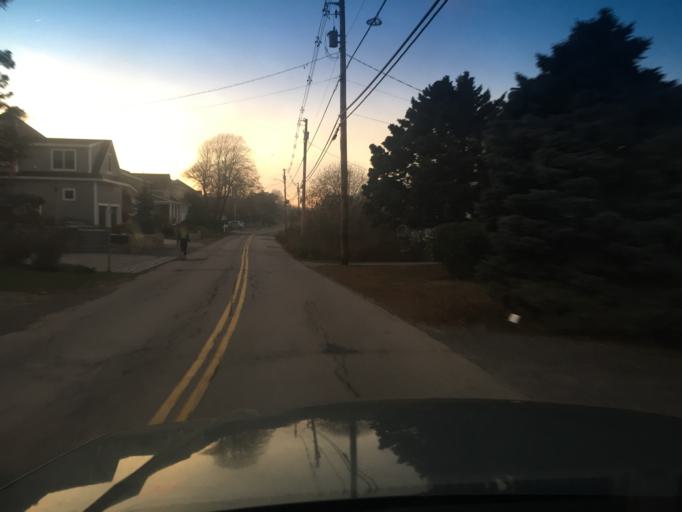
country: US
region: Maine
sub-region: York County
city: York Beach
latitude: 43.1679
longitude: -70.6045
